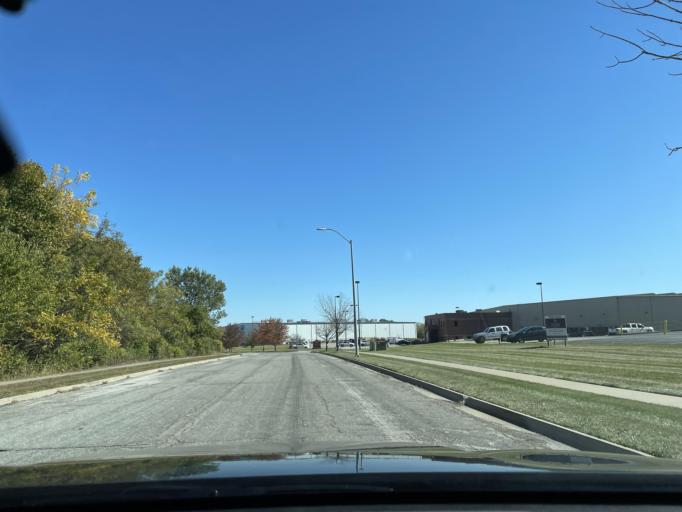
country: US
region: Missouri
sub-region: Buchanan County
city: Saint Joseph
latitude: 39.7508
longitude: -94.7596
